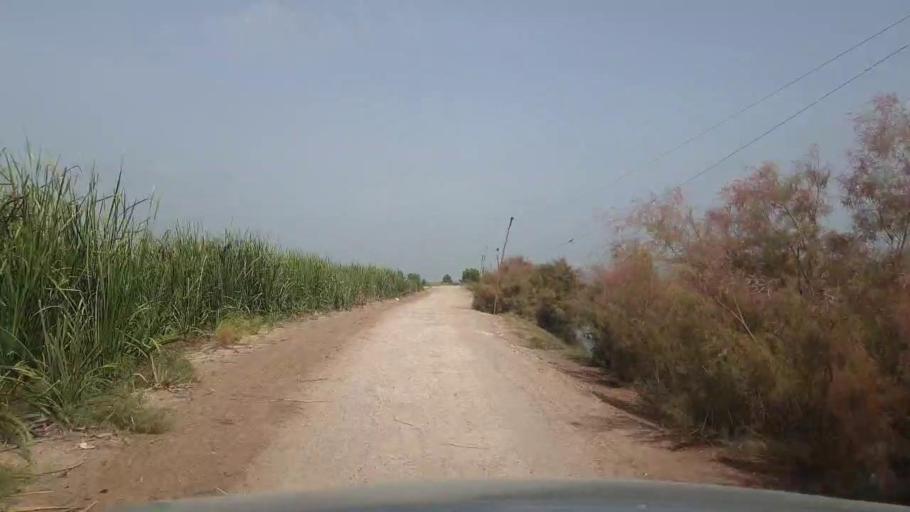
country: PK
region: Sindh
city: Garhi Yasin
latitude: 27.9572
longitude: 68.3638
